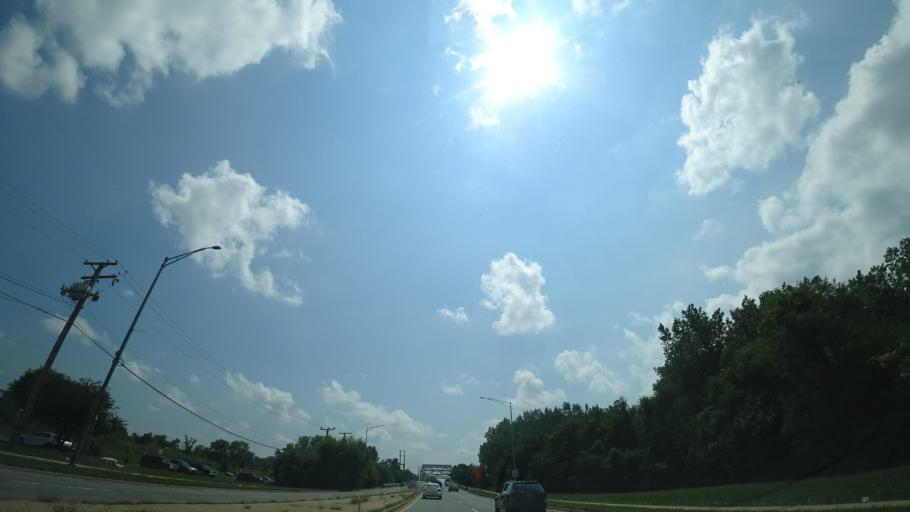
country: US
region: Illinois
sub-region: Cook County
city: Worth
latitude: 41.6801
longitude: -87.7971
